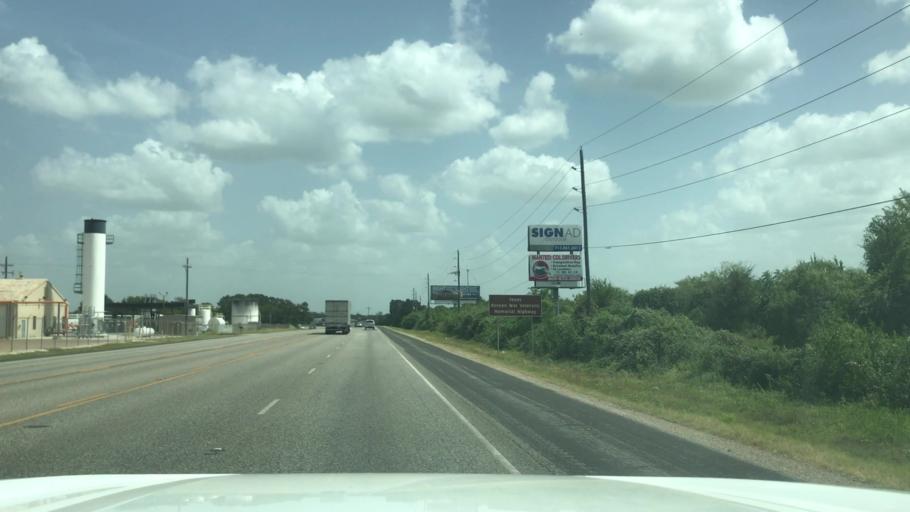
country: US
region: Texas
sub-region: Robertson County
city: Hearne
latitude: 30.8638
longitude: -96.5820
